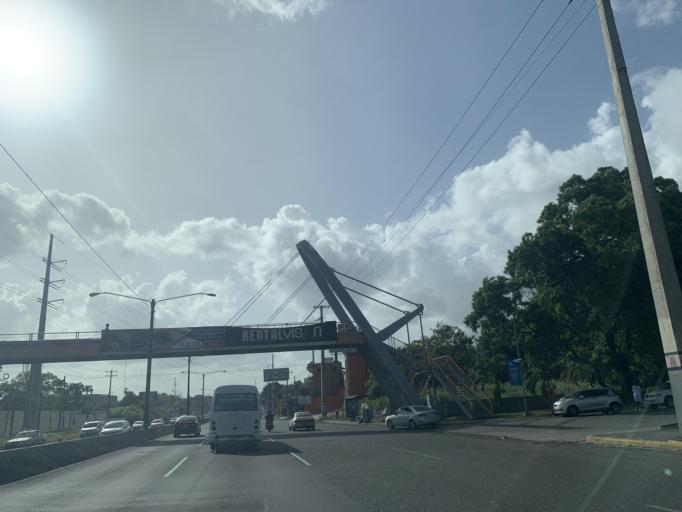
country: DO
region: Nacional
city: Santo Domingo
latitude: 18.4932
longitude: -69.9859
